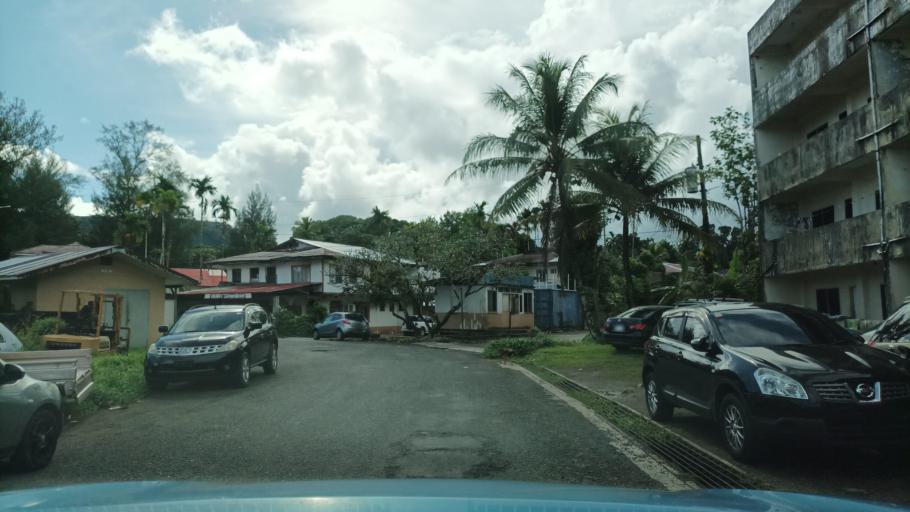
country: FM
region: Pohnpei
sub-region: Kolonia Municipality
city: Kolonia
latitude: 6.9630
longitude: 158.2155
